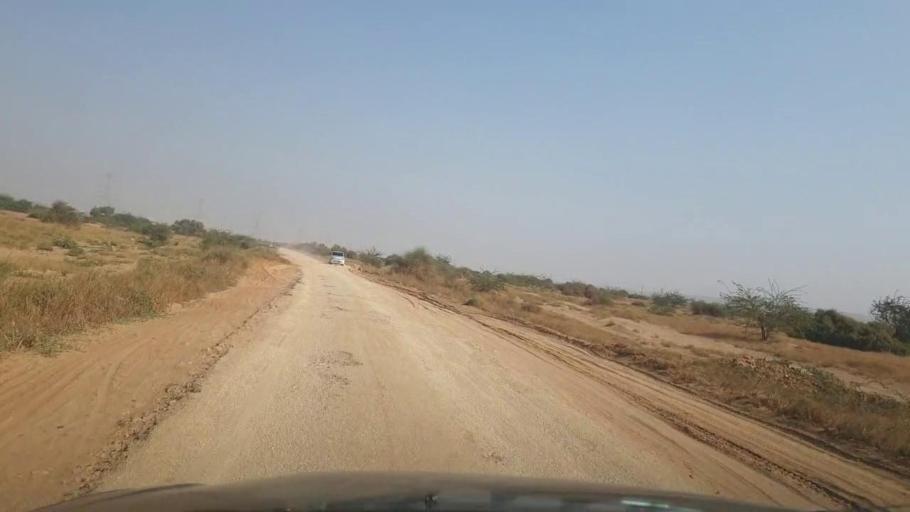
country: PK
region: Sindh
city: Gharo
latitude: 25.2272
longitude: 67.6755
